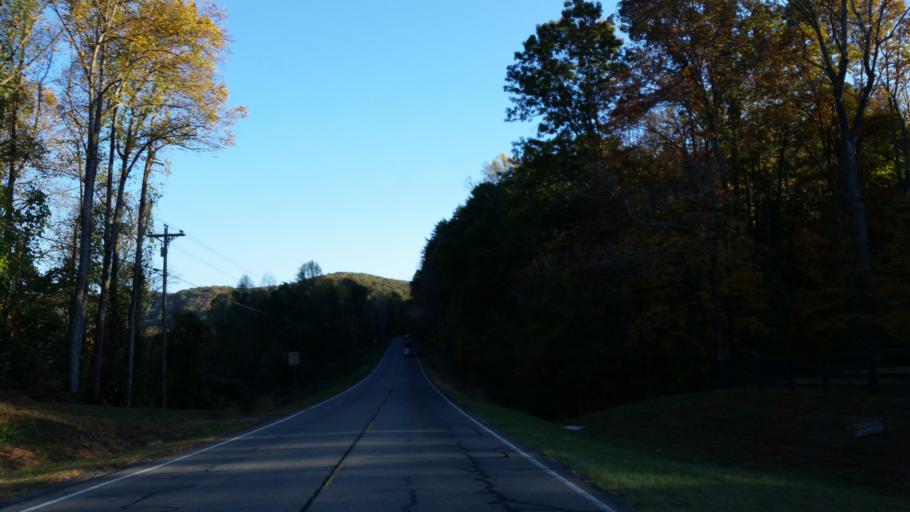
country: US
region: Georgia
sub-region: Pickens County
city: Jasper
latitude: 34.5843
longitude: -84.3047
